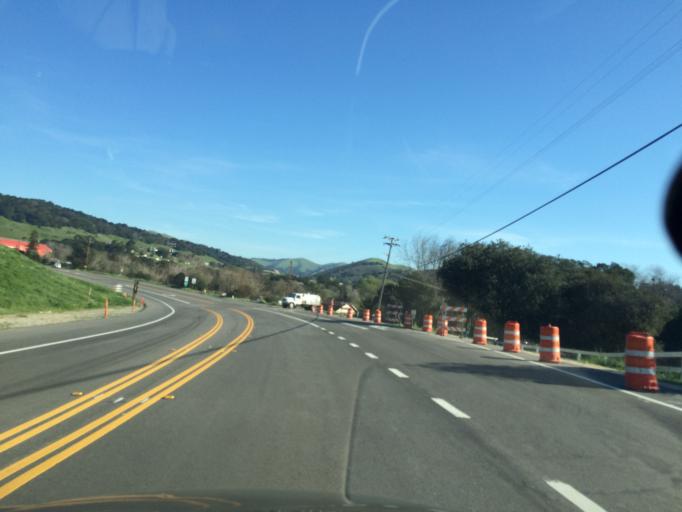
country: US
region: California
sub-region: San Benito County
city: Aromas
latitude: 36.8551
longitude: -121.6402
